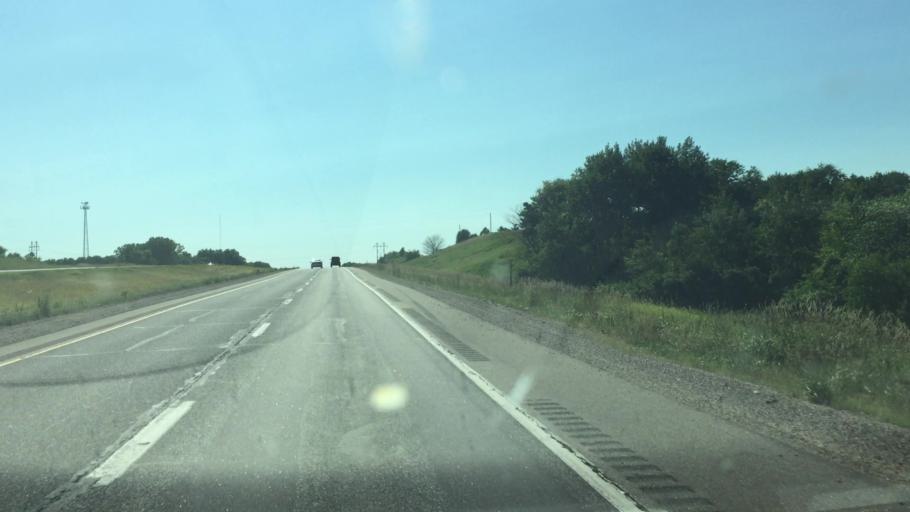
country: US
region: Iowa
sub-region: Linn County
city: Ely
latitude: 41.9260
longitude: -91.5887
